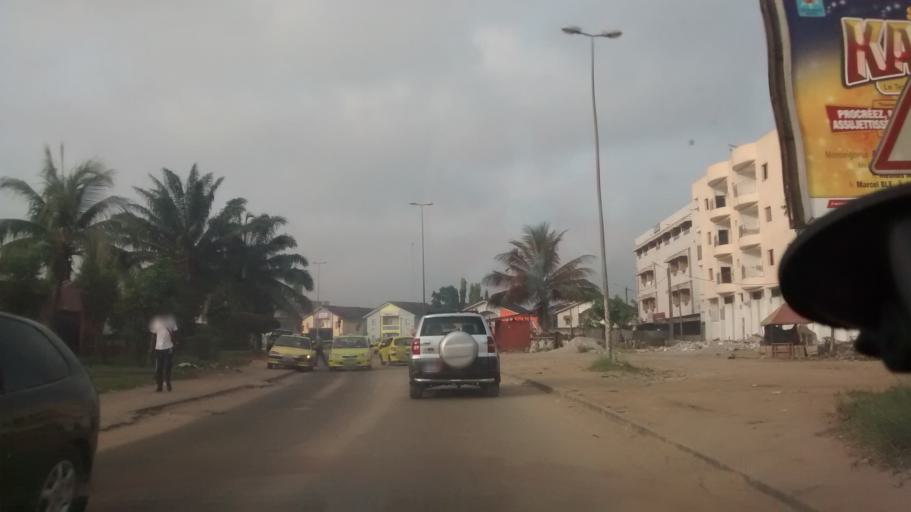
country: CI
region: Lagunes
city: Abobo
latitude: 5.4070
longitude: -3.9896
